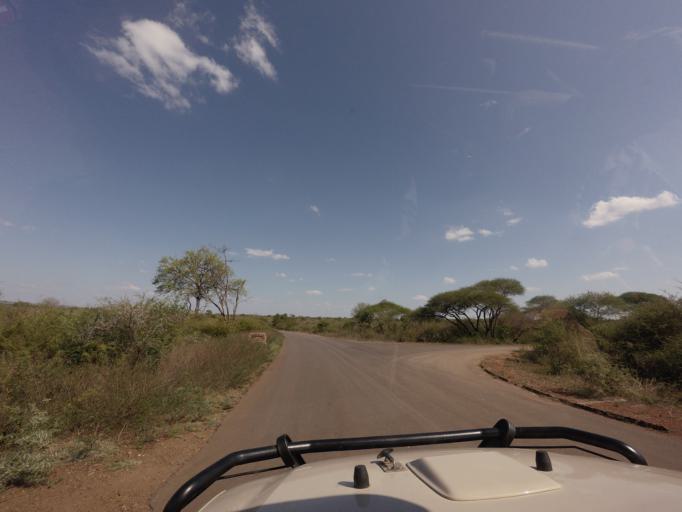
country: ZA
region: Mpumalanga
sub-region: Ehlanzeni District
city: Komatipoort
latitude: -25.1238
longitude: 31.9151
